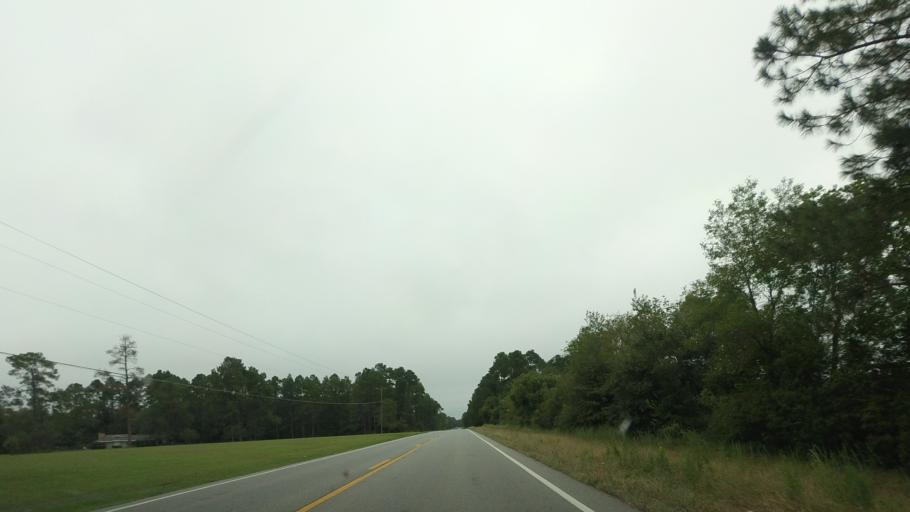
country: US
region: Georgia
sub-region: Berrien County
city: Nashville
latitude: 31.2409
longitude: -83.2445
